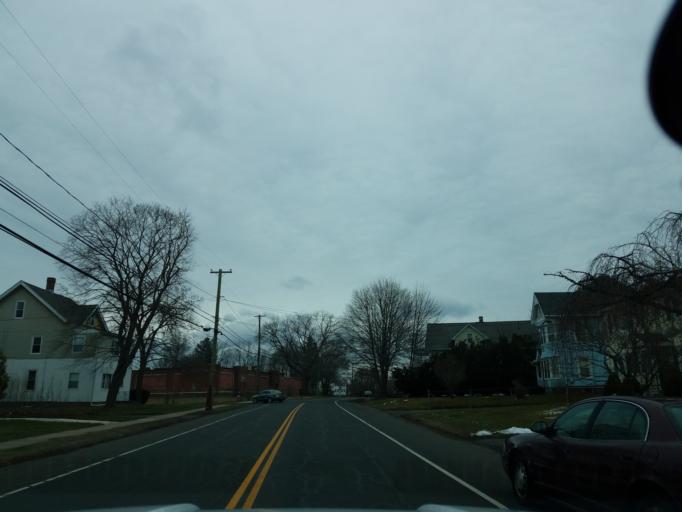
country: US
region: Connecticut
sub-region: Hartford County
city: New Britain
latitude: 41.6844
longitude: -72.7911
